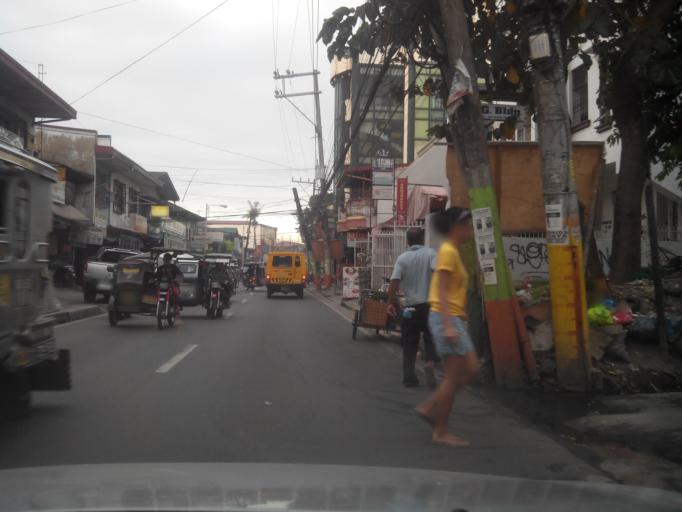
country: PH
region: Calabarzon
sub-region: Province of Rizal
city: Cainta
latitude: 14.5716
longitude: 121.1292
